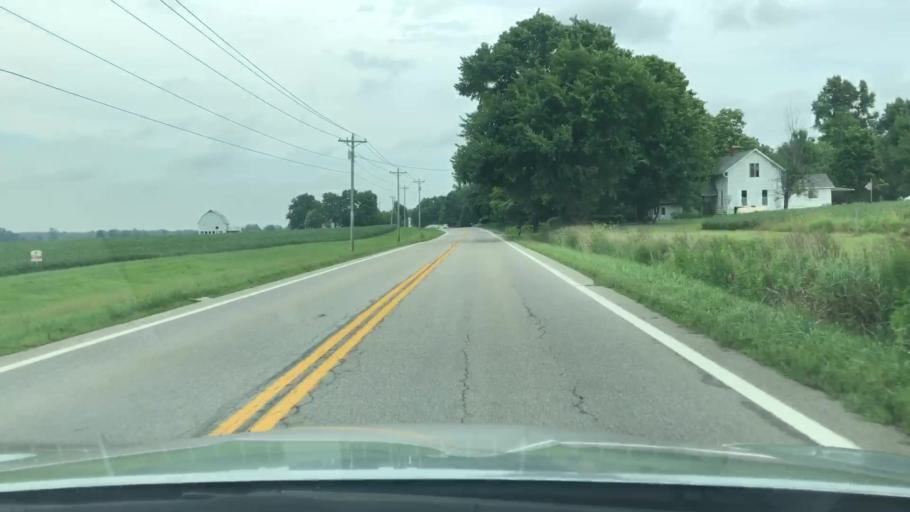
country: US
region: Ohio
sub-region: Delaware County
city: Sunbury
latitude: 40.3452
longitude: -82.8323
